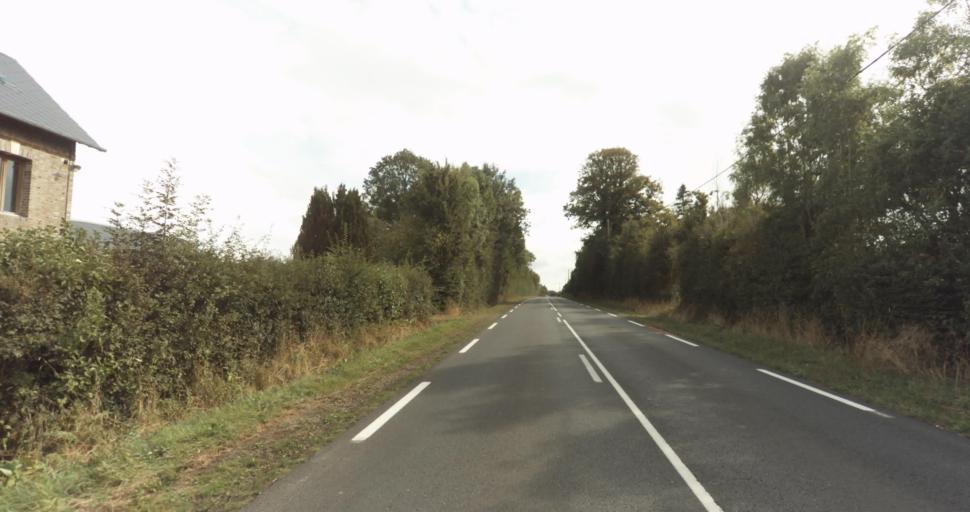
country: FR
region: Lower Normandy
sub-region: Departement de l'Orne
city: Gace
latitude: 48.8614
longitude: 0.2529
